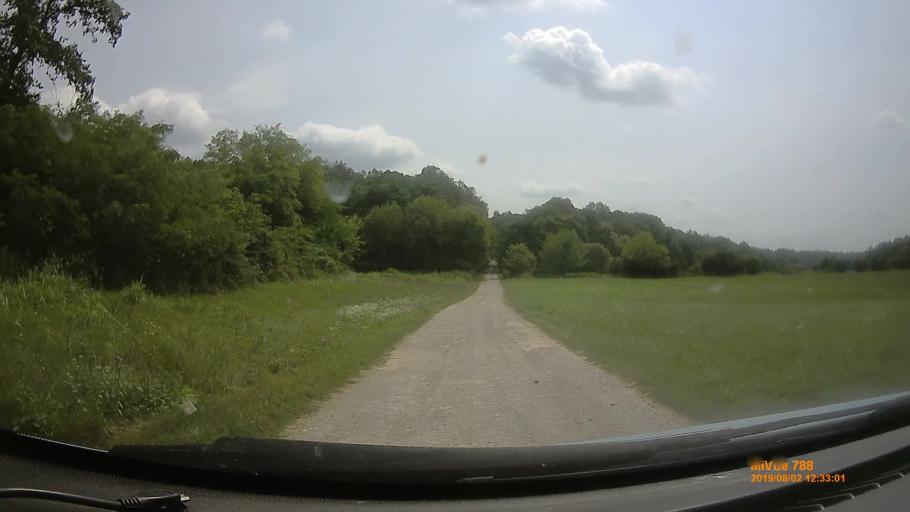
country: HU
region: Baranya
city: Buekkoesd
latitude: 46.1016
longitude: 17.9413
